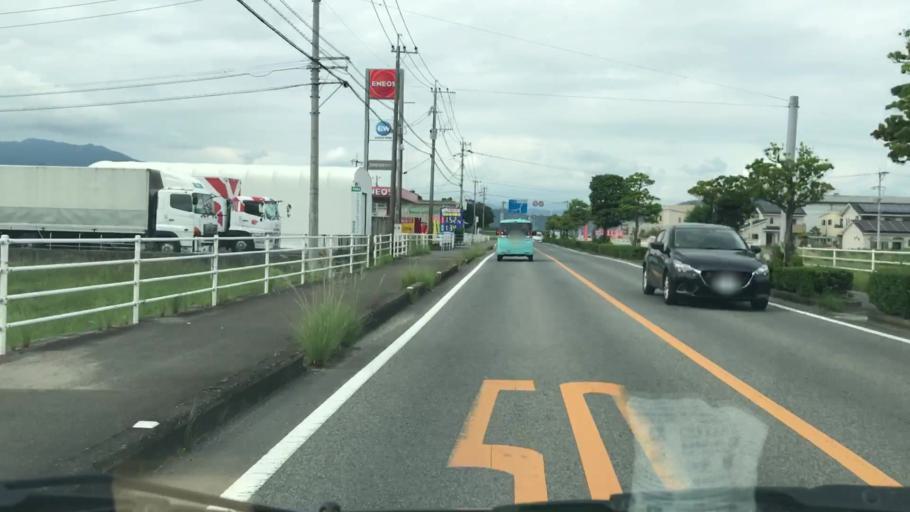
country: JP
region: Saga Prefecture
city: Saga-shi
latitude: 33.2737
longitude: 130.2609
